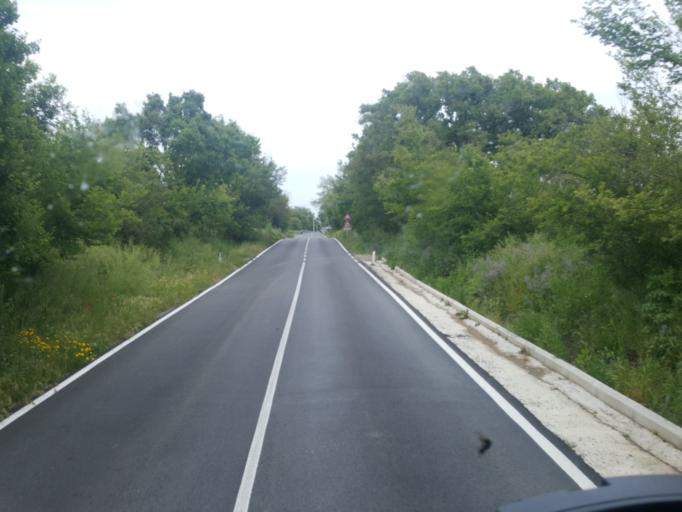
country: IT
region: Latium
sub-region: Provincia di Viterbo
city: Monte Romano
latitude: 42.2801
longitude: 11.9194
